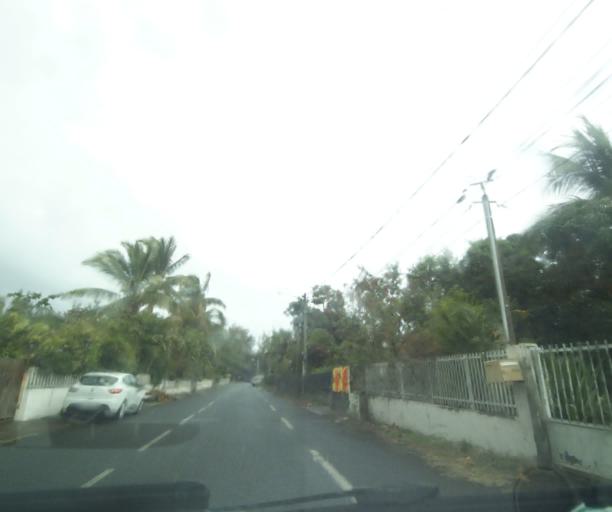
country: RE
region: Reunion
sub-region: Reunion
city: Saint-Paul
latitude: -20.9903
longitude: 55.2840
